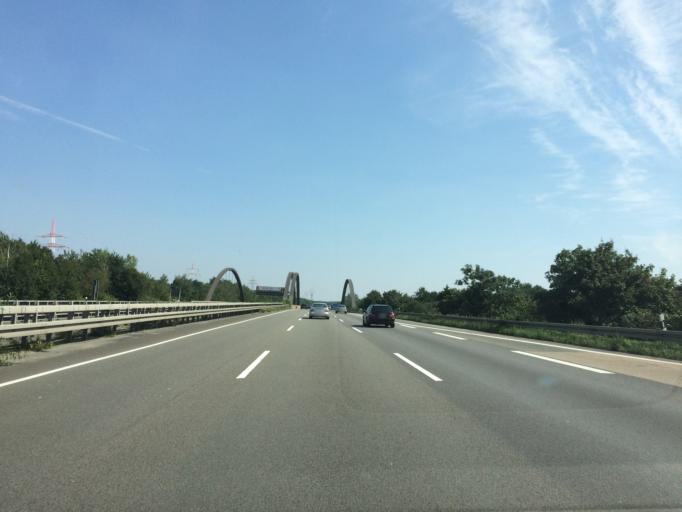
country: DE
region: North Rhine-Westphalia
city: Waltrop
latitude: 51.5836
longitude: 7.4046
